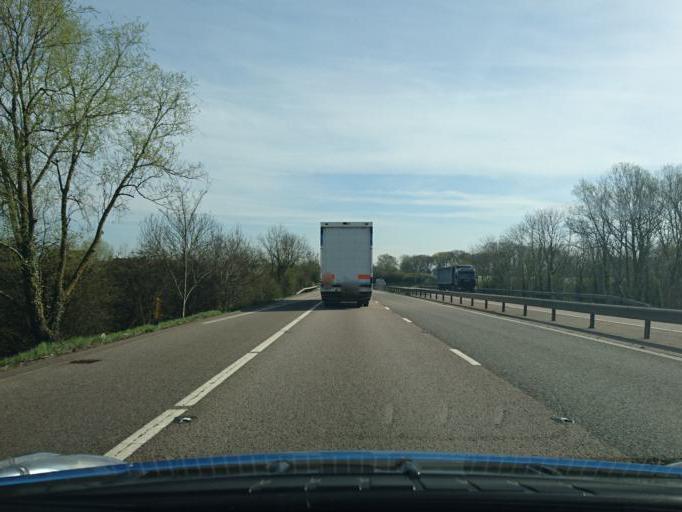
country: GB
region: England
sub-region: Worcestershire
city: Upton upon Severn
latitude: 52.0197
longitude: -2.2194
